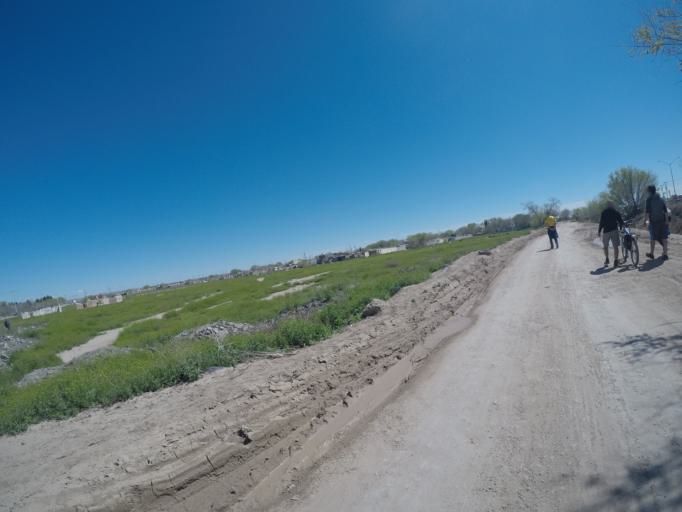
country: US
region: Texas
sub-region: El Paso County
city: Socorro Mission Number 1 Colonia
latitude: 31.6176
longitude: -106.3197
